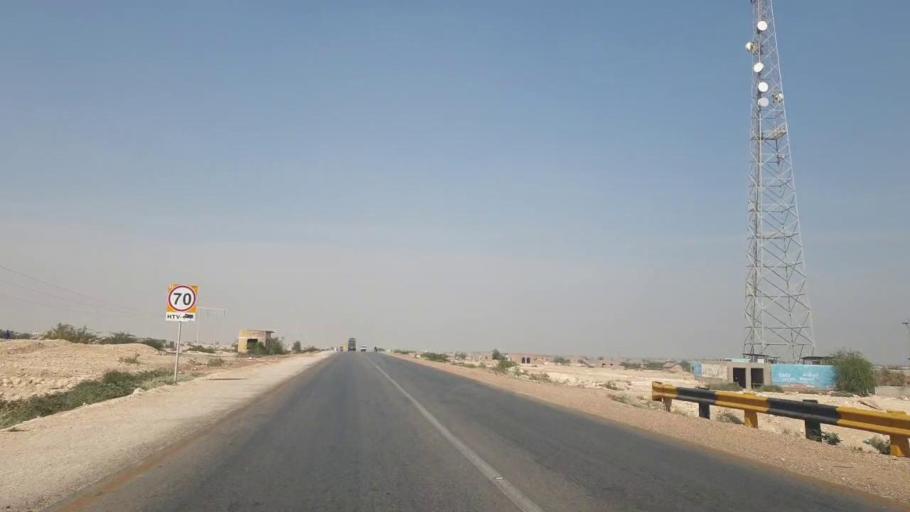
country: PK
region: Sindh
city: Hala
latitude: 25.7733
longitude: 68.2855
